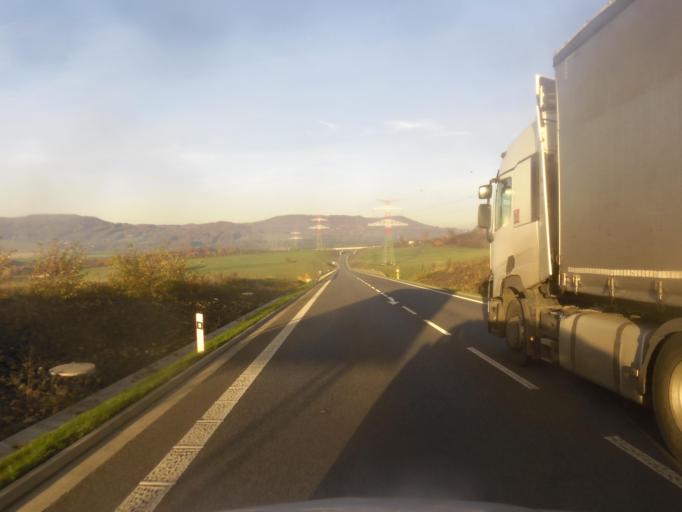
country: CZ
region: Ustecky
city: Ustek
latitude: 50.6246
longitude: 14.3950
